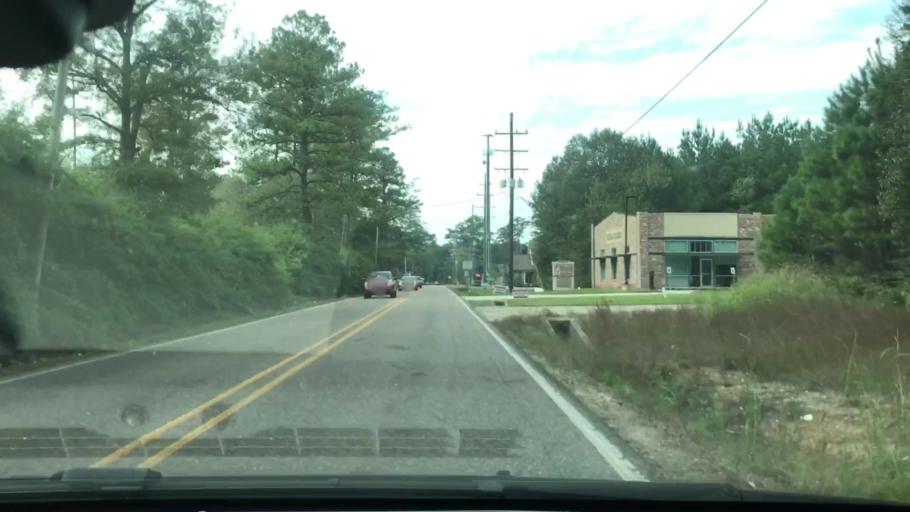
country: US
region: Louisiana
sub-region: Saint Tammany Parish
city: Abita Springs
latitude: 30.4824
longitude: -90.0415
